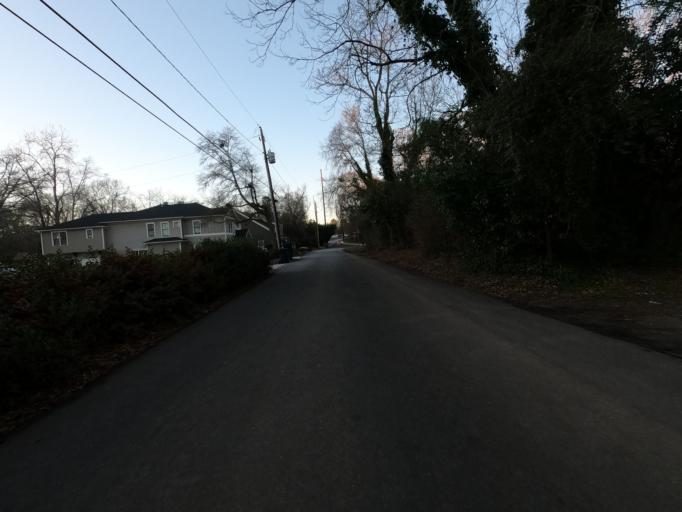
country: US
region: Georgia
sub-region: Clarke County
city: Athens
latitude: 33.9296
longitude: -83.3924
